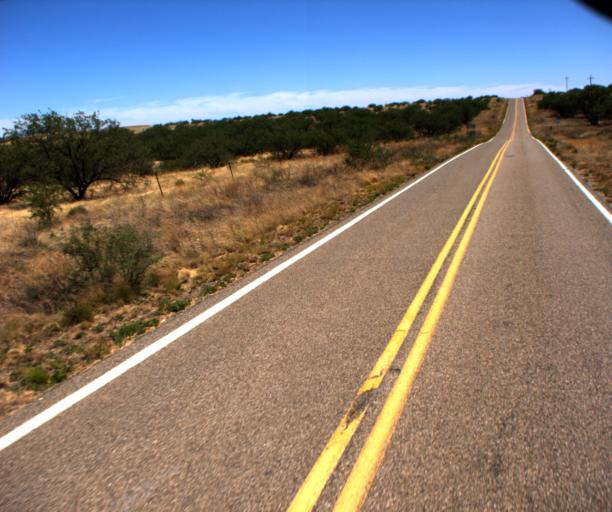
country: US
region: Arizona
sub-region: Pima County
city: Sells
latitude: 31.5679
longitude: -111.5383
